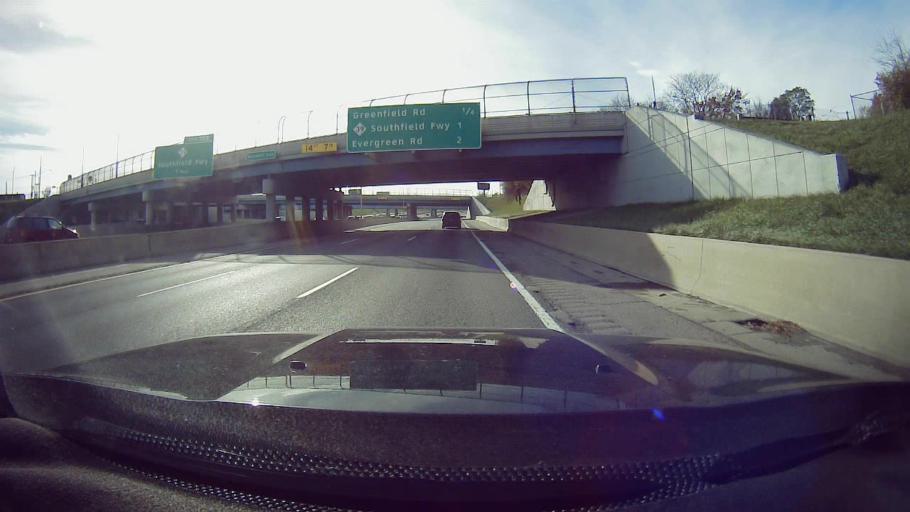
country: US
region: Michigan
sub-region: Wayne County
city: Dearborn
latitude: 42.3811
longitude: -83.1877
